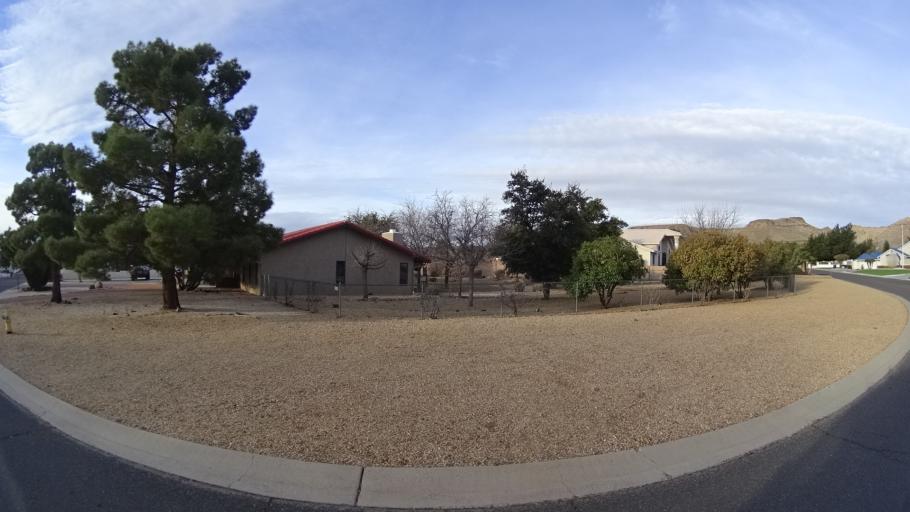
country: US
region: Arizona
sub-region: Mohave County
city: New Kingman-Butler
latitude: 35.2432
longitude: -114.0441
